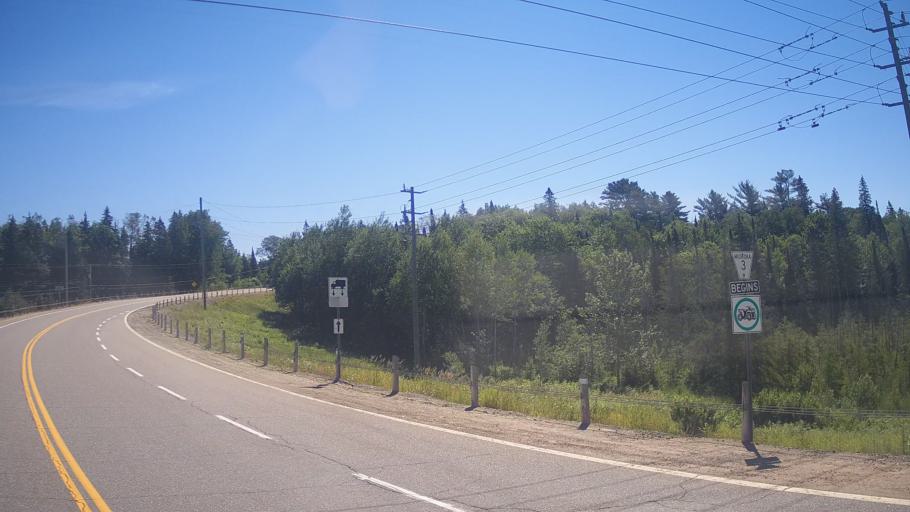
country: CA
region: Ontario
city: Huntsville
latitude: 45.3733
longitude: -79.2142
